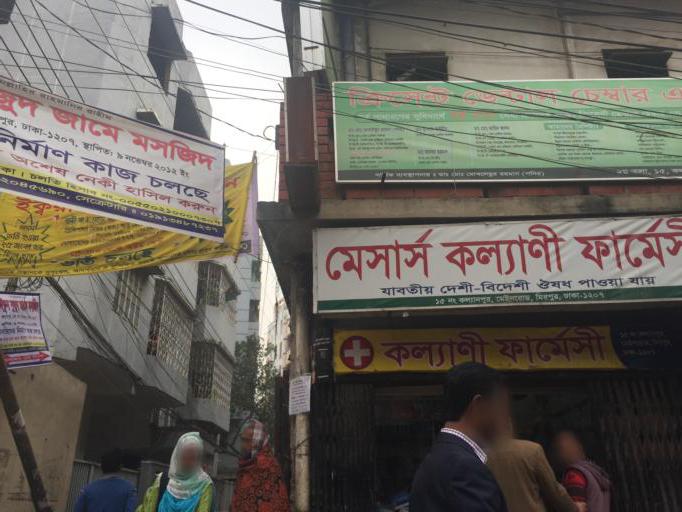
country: BD
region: Dhaka
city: Azimpur
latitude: 23.7793
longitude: 90.3612
